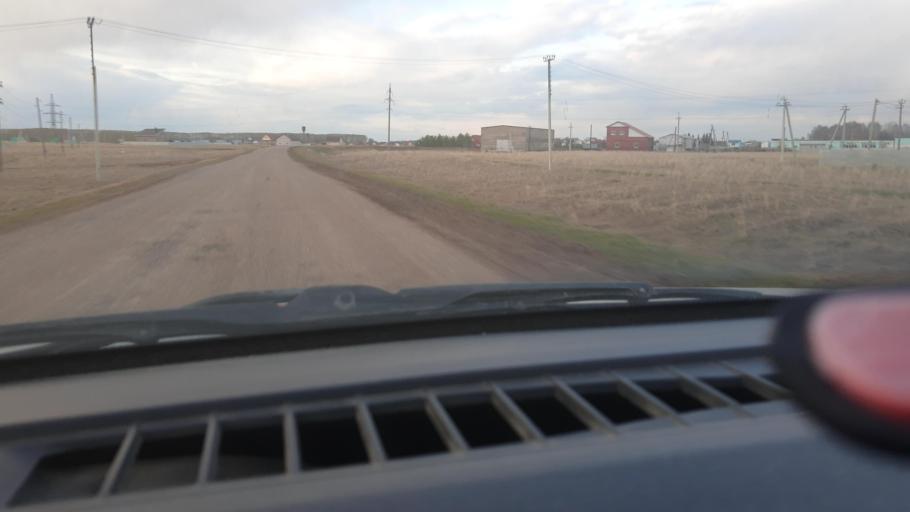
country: RU
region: Bashkortostan
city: Asanovo
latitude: 54.9564
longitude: 55.5343
